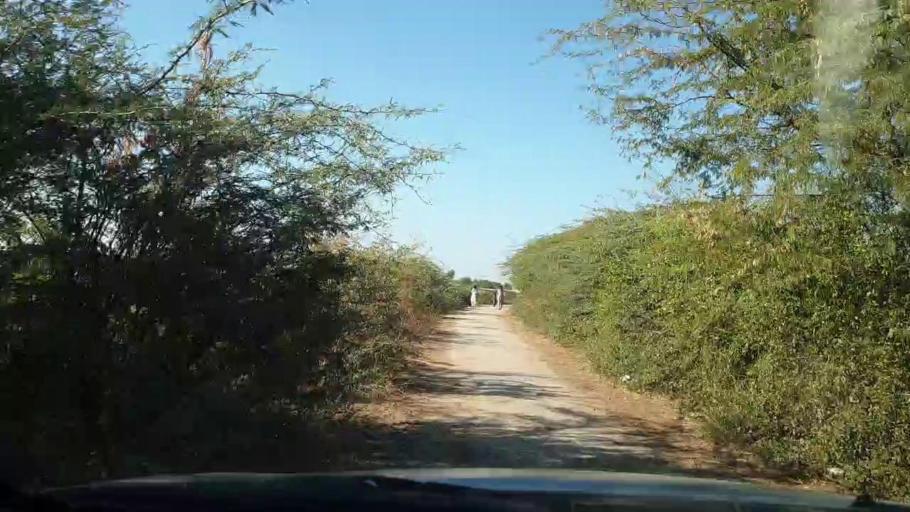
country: PK
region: Sindh
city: Berani
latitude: 25.8183
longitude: 68.9426
